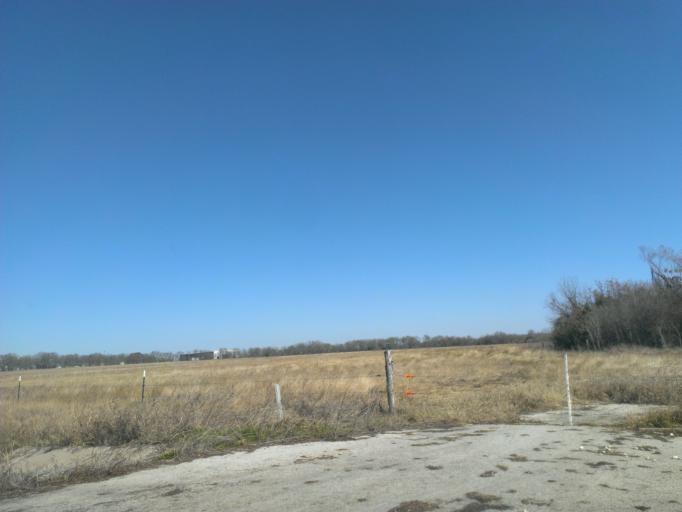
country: US
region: Texas
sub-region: Williamson County
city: Georgetown
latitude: 30.6711
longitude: -97.5844
